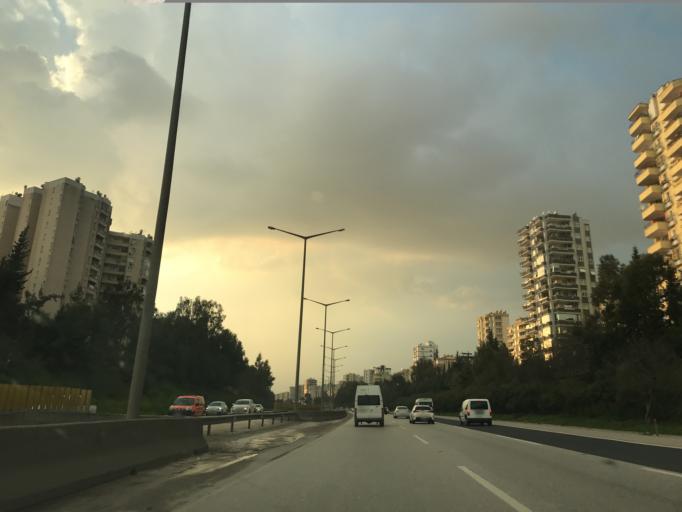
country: TR
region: Adana
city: Adana
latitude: 37.0312
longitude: 35.3094
